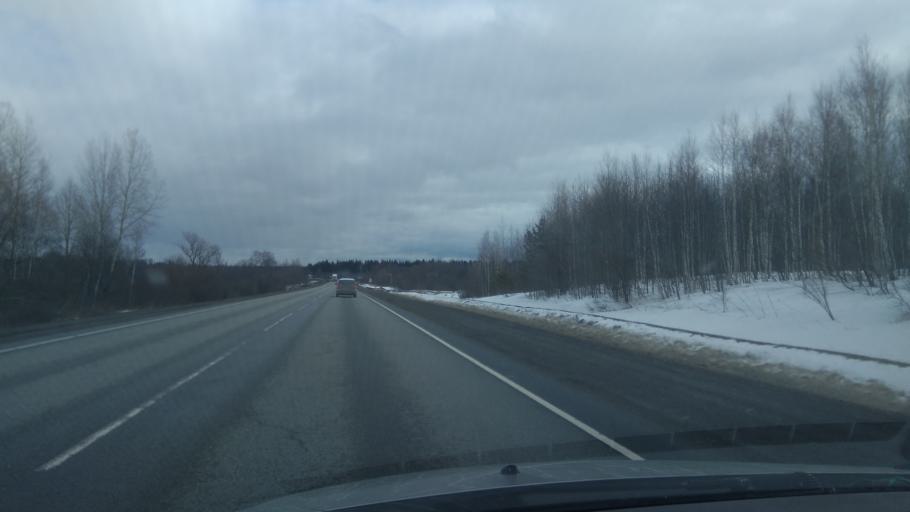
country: RU
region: Sverdlovsk
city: Ufimskiy
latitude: 56.7716
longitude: 58.0806
